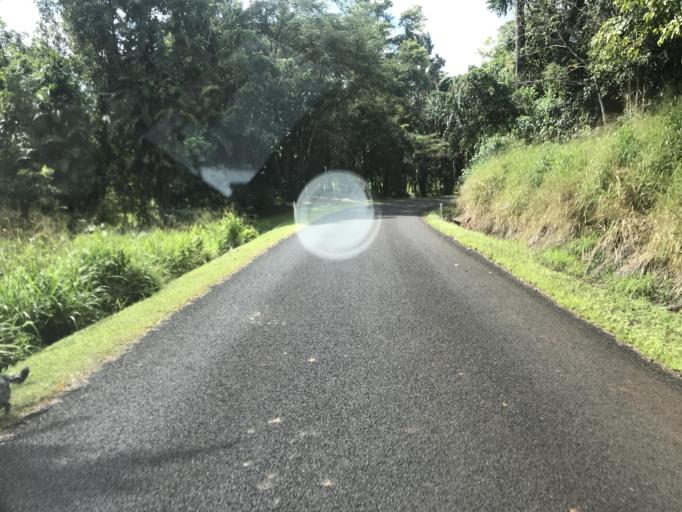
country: AU
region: Queensland
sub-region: Cassowary Coast
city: Innisfail
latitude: -17.5501
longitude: 145.8680
